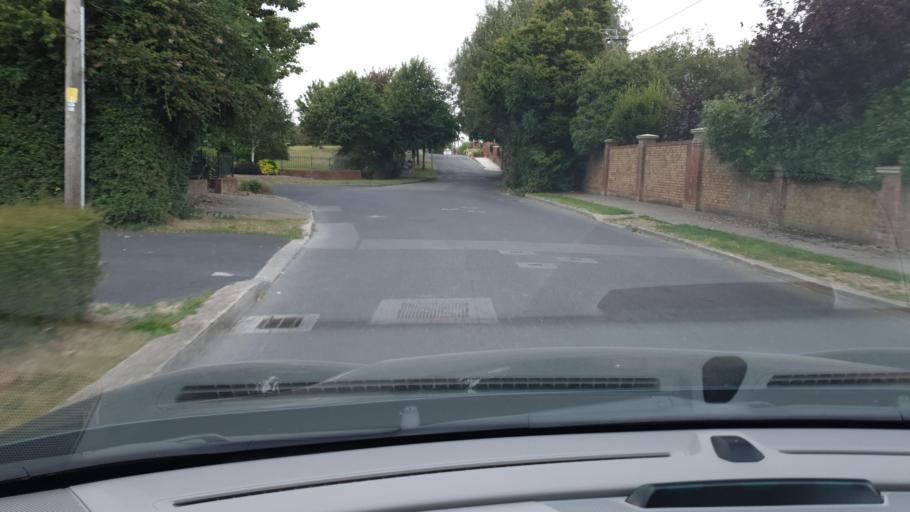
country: IE
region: Leinster
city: Donabate
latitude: 53.4950
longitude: -6.1448
